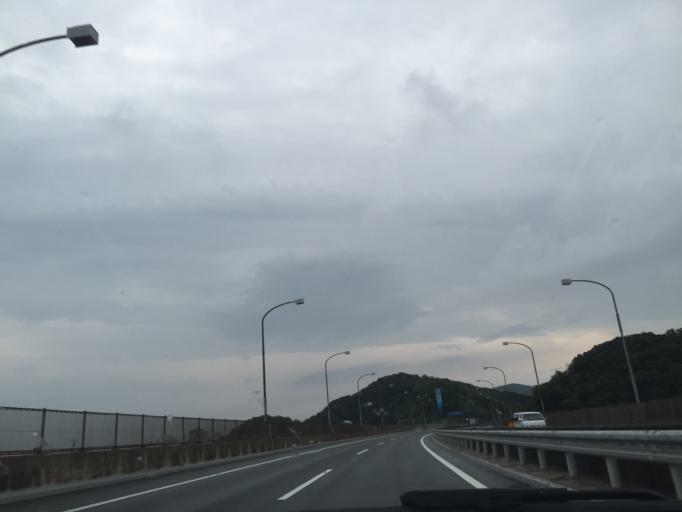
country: JP
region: Tokushima
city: Narutocho-mitsuishi
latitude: 34.1904
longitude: 134.6118
